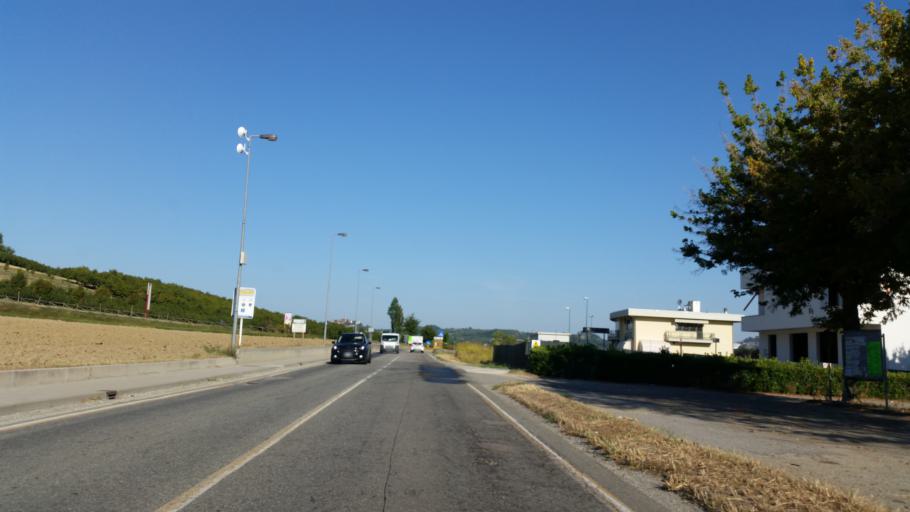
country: IT
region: Piedmont
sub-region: Provincia di Cuneo
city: Roddi
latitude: 44.6818
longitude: 7.9829
